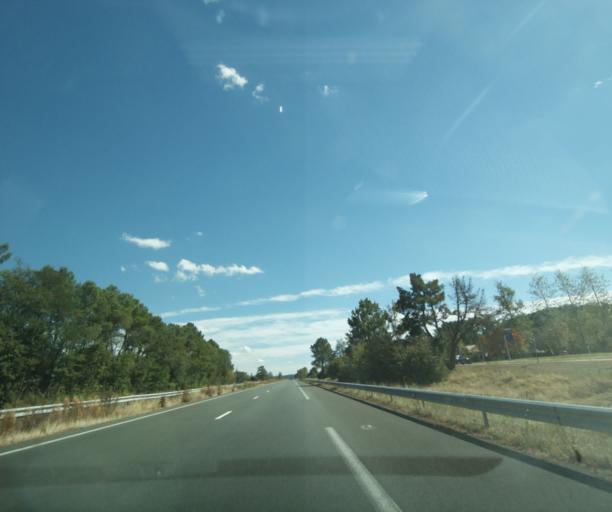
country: FR
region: Aquitaine
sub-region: Departement du Lot-et-Garonne
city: Buzet-sur-Baise
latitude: 44.2507
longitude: 0.2998
